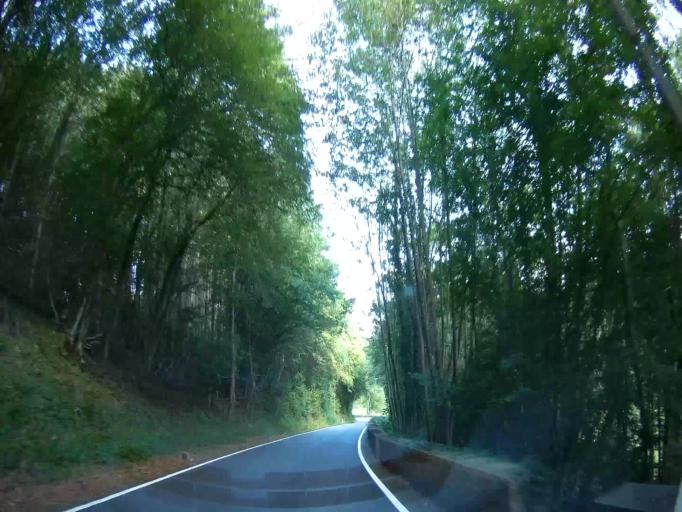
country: BE
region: Wallonia
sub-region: Province de Namur
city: Onhaye
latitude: 50.3042
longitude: 4.7764
